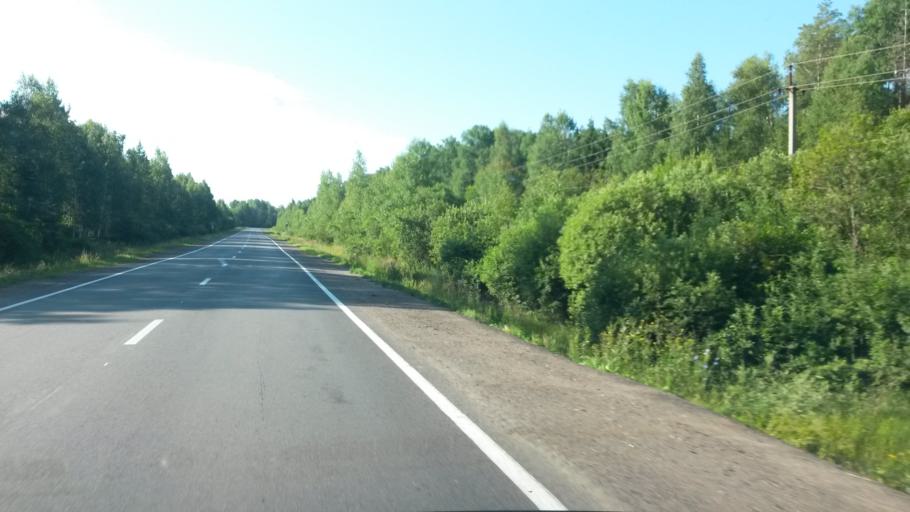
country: RU
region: Jaroslavl
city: Gavrilov-Yam
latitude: 57.2923
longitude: 39.9502
